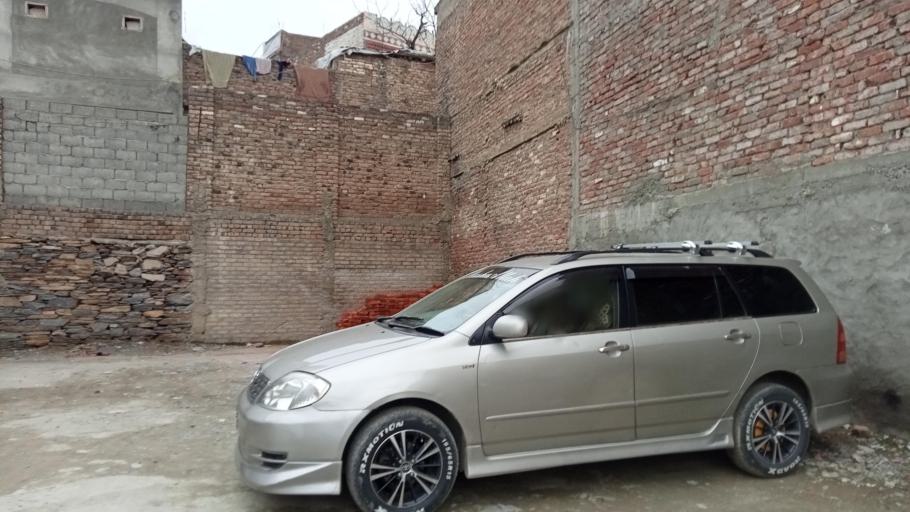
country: PK
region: Khyber Pakhtunkhwa
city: Mingora
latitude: 34.7679
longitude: 72.3405
